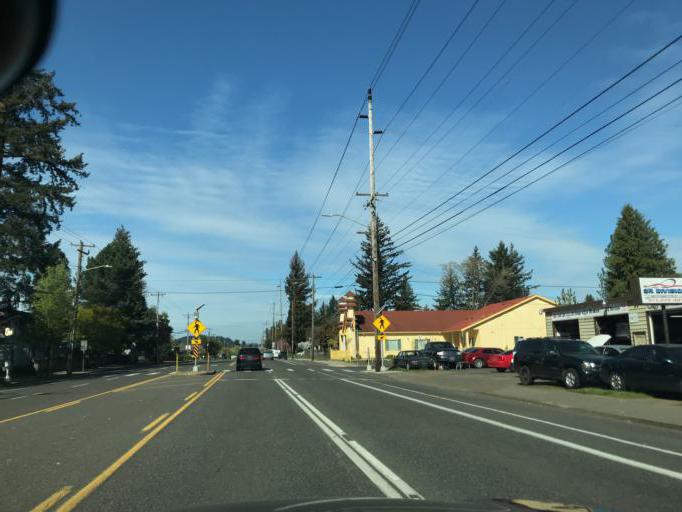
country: US
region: Oregon
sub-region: Clackamas County
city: Happy Valley
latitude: 45.5044
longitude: -122.5024
